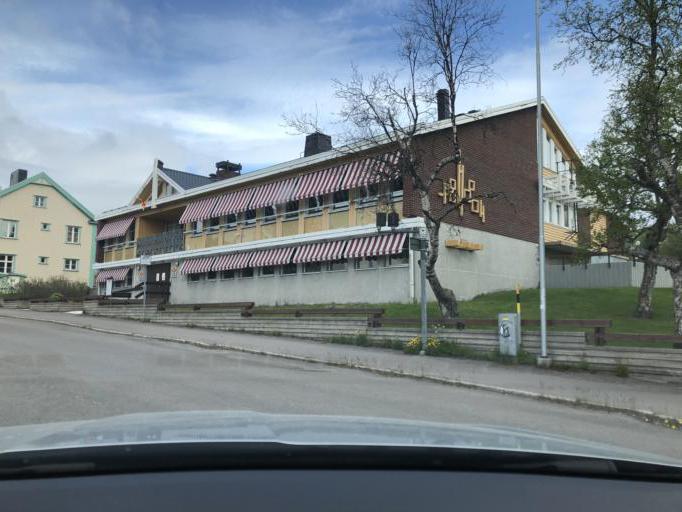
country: SE
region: Norrbotten
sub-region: Kiruna Kommun
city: Kiruna
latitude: 67.8518
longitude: 20.2370
